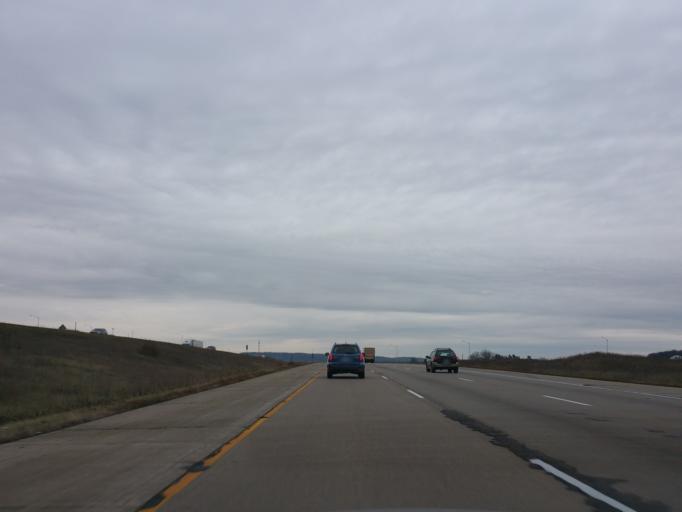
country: US
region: Wisconsin
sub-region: Columbia County
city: Poynette
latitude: 43.4286
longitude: -89.4810
